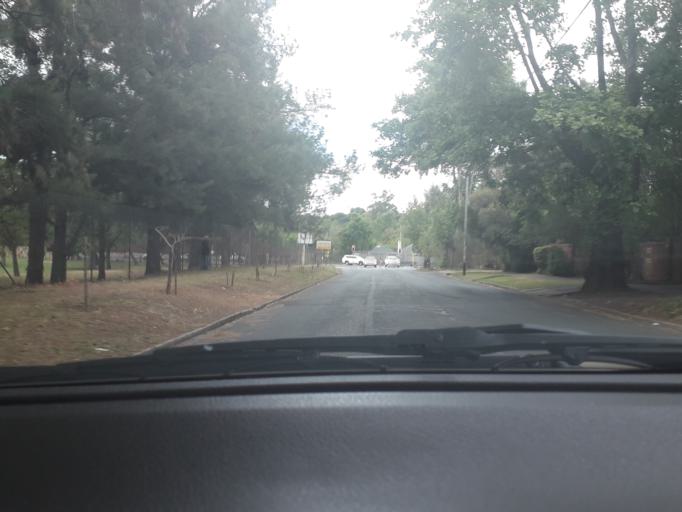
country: ZA
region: Gauteng
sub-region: City of Johannesburg Metropolitan Municipality
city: Johannesburg
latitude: -26.1527
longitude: 28.0218
